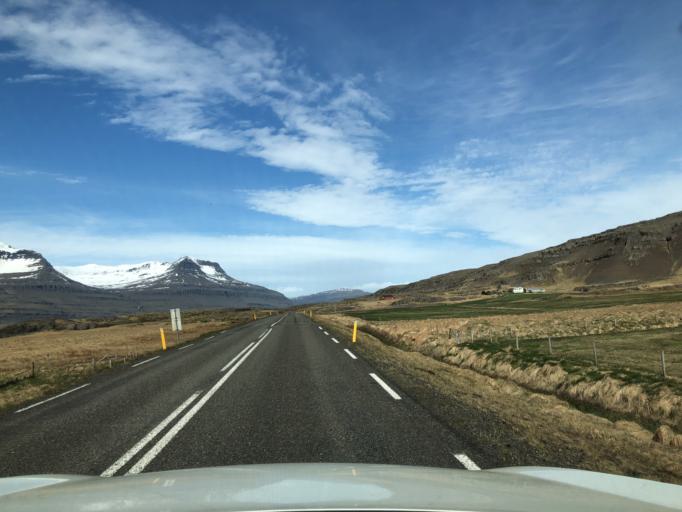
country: IS
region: East
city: Reydarfjoerdur
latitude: 64.6978
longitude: -14.2702
